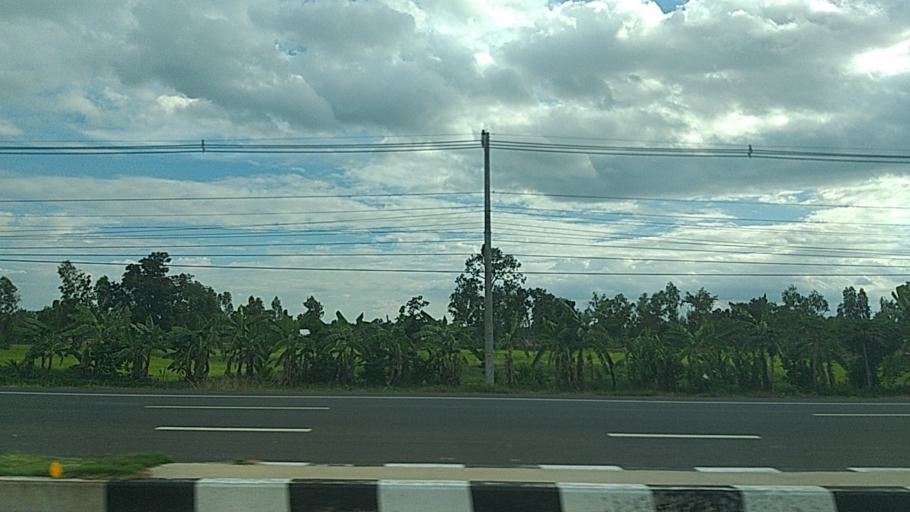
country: TH
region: Surin
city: Prasat
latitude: 14.5658
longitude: 103.4931
